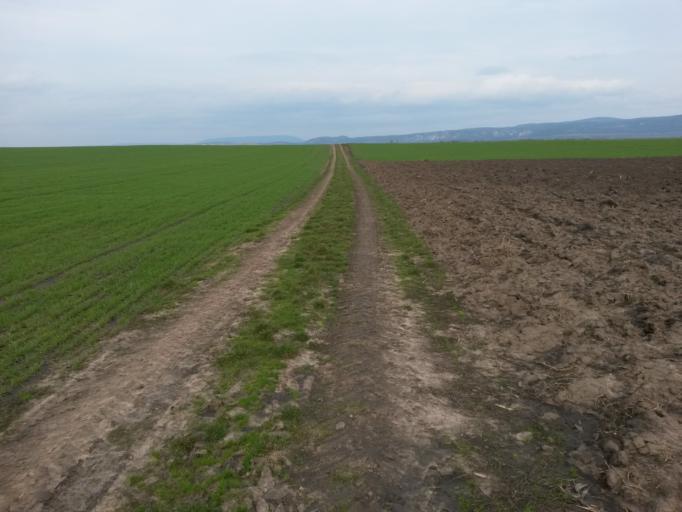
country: HU
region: Pest
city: Zsambek
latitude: 47.5524
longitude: 18.7548
